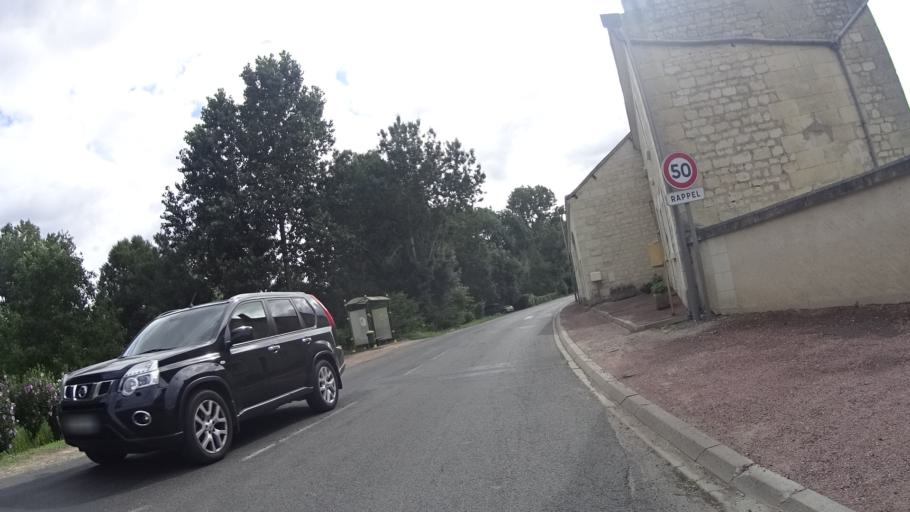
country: FR
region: Centre
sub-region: Departement d'Indre-et-Loire
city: Avoine
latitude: 47.2317
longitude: 0.1951
